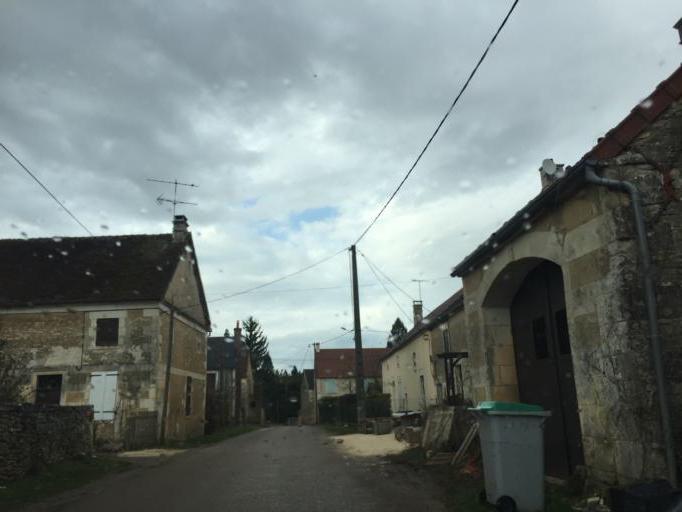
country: FR
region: Bourgogne
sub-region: Departement de l'Yonne
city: Fontenailles
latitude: 47.5425
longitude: 3.3374
